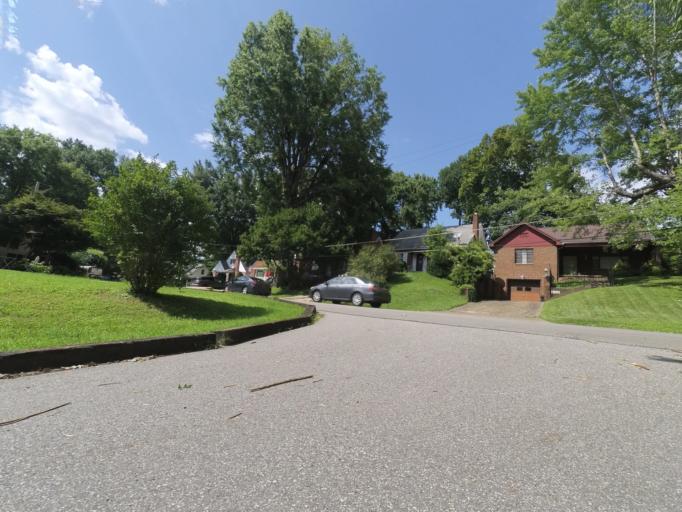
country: US
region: West Virginia
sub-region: Cabell County
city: Huntington
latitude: 38.4067
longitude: -82.4257
